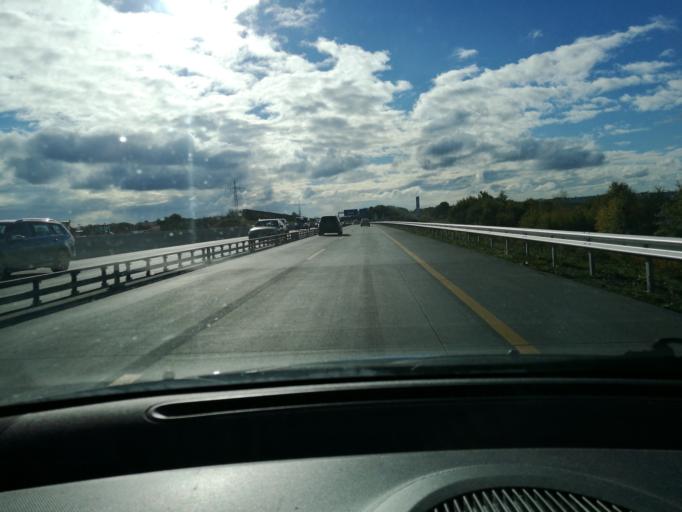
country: DE
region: Schleswig-Holstein
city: Wasbek
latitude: 54.0773
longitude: 9.9241
